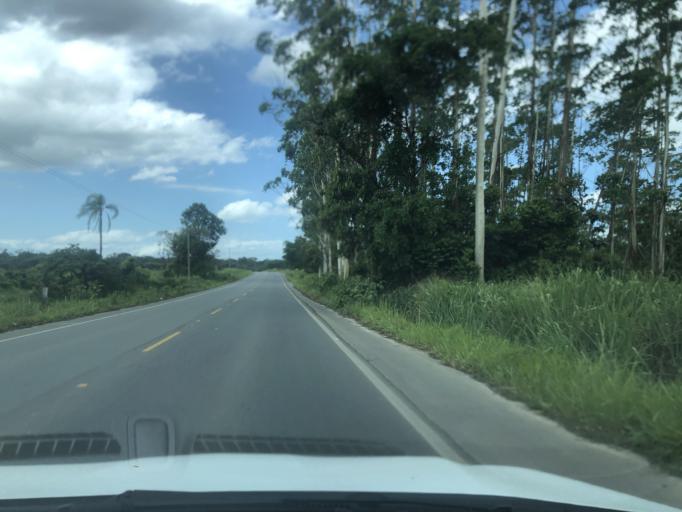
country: BR
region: Santa Catarina
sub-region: Joinville
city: Joinville
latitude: -26.4061
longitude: -48.7585
